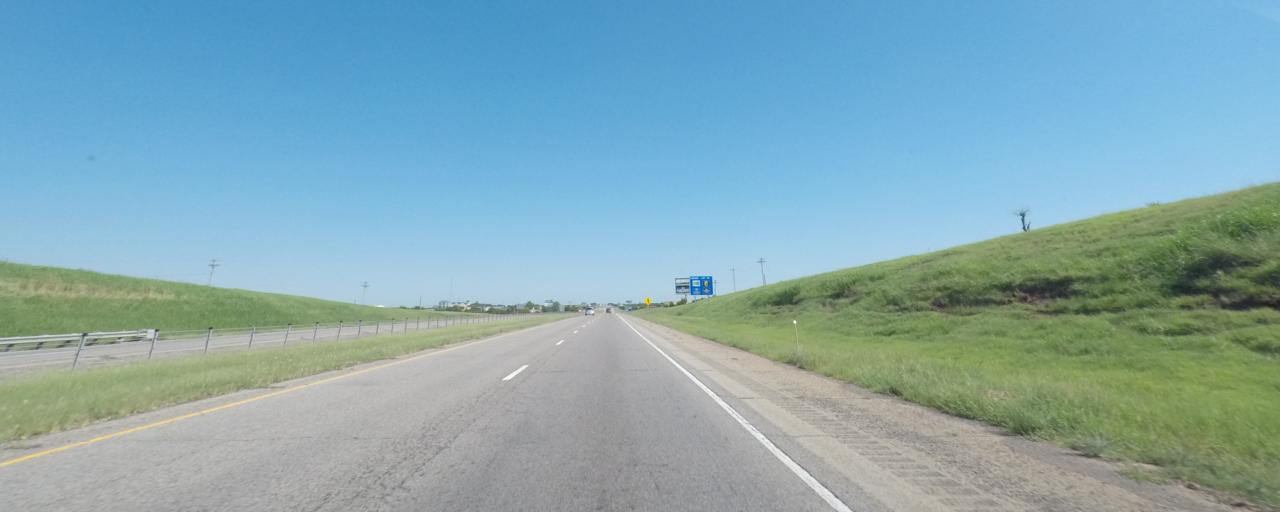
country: US
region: Oklahoma
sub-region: Noble County
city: Perry
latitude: 36.2754
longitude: -97.3276
